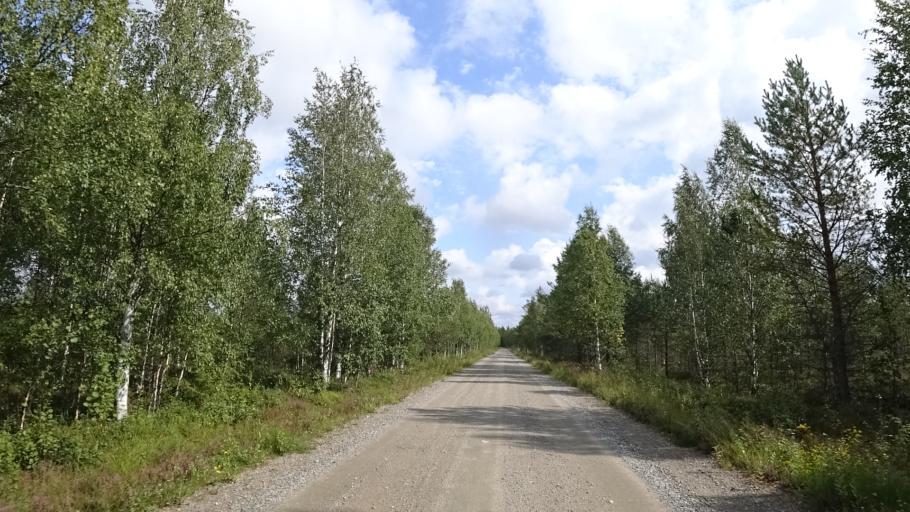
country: FI
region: North Karelia
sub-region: Joensuu
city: Ilomantsi
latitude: 62.9271
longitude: 31.4006
